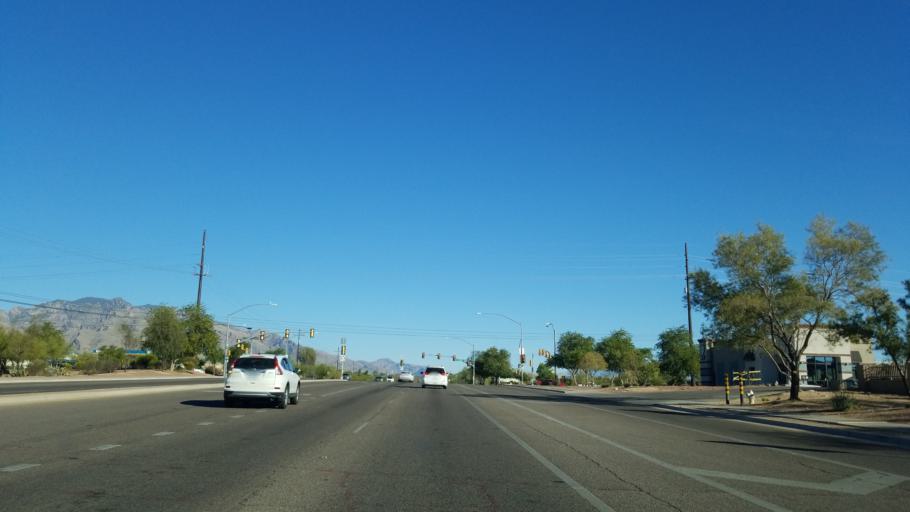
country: US
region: Arizona
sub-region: Pima County
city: Casas Adobes
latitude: 32.3231
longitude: -111.0138
